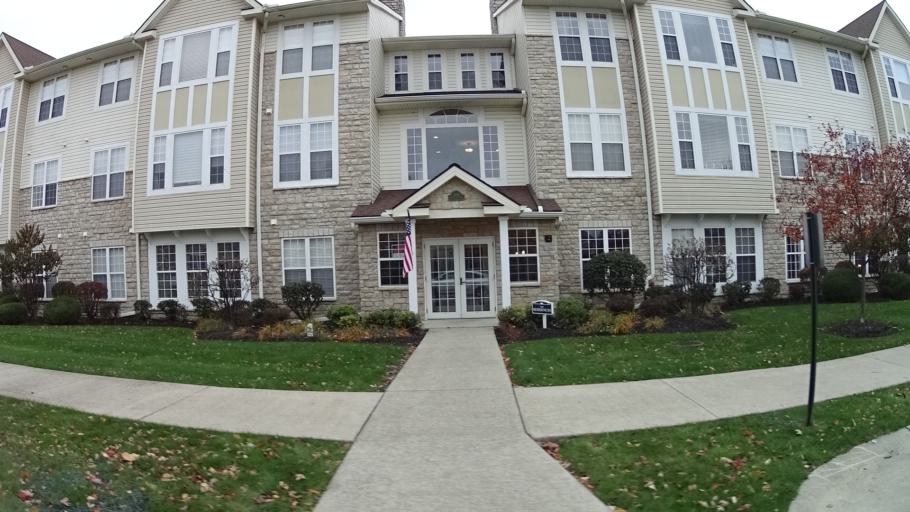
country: US
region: Ohio
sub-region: Lorain County
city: Amherst
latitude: 41.4393
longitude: -82.2303
